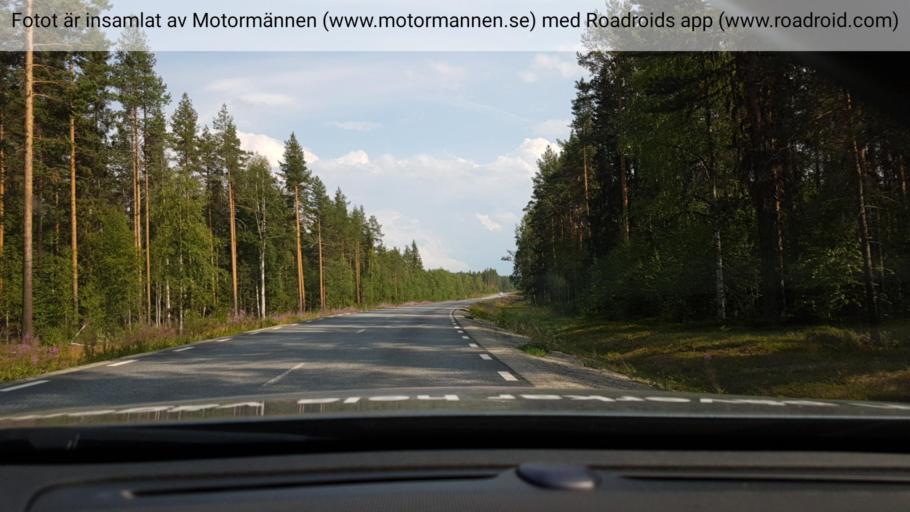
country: SE
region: Vaesterbotten
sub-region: Bjurholms Kommun
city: Bjurholm
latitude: 64.3859
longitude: 19.1080
